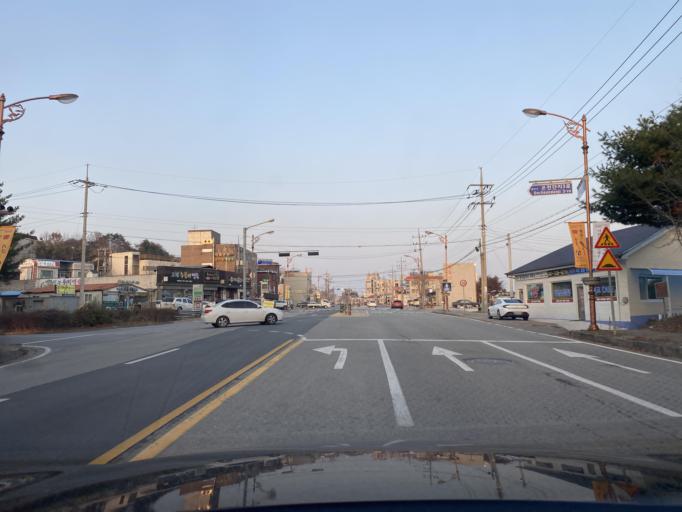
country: KR
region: Chungcheongnam-do
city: Hongsung
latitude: 36.6928
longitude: 126.6600
